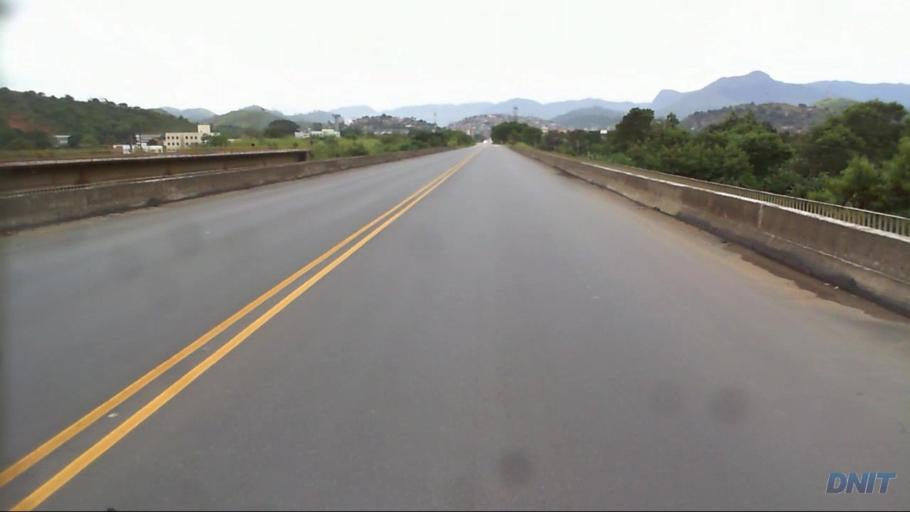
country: BR
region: Minas Gerais
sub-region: Coronel Fabriciano
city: Coronel Fabriciano
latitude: -19.5317
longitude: -42.6014
